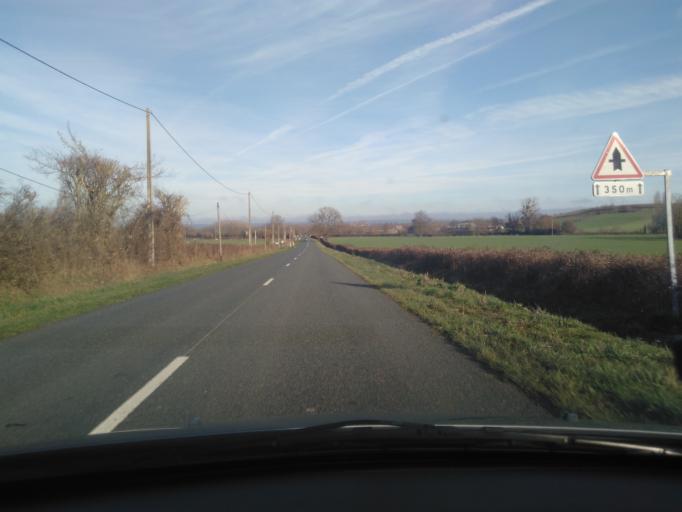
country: FR
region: Centre
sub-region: Departement du Cher
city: Orval
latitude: 46.6827
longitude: 2.4635
